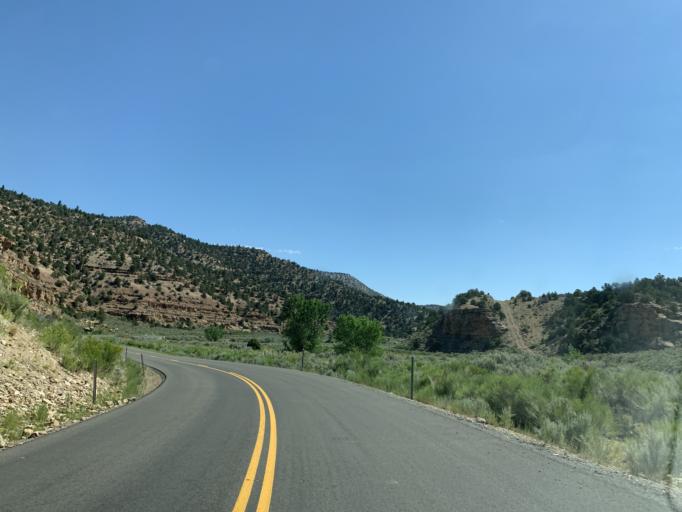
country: US
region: Utah
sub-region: Carbon County
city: East Carbon City
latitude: 39.7779
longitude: -110.4322
